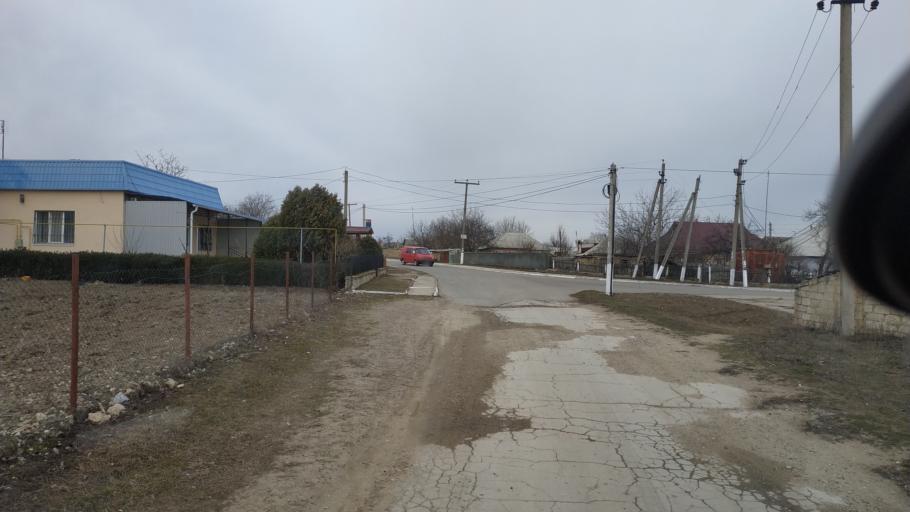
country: MD
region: Telenesti
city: Cocieri
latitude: 47.2558
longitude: 29.0607
